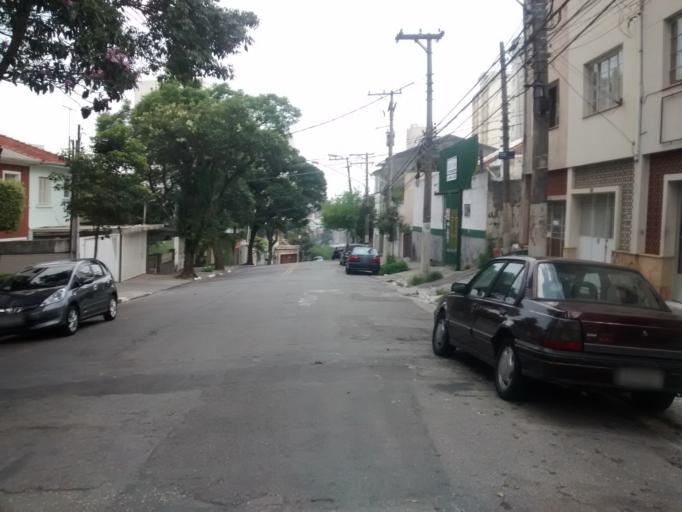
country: BR
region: Sao Paulo
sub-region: Sao Paulo
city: Sao Paulo
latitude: -23.6129
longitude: -46.6333
